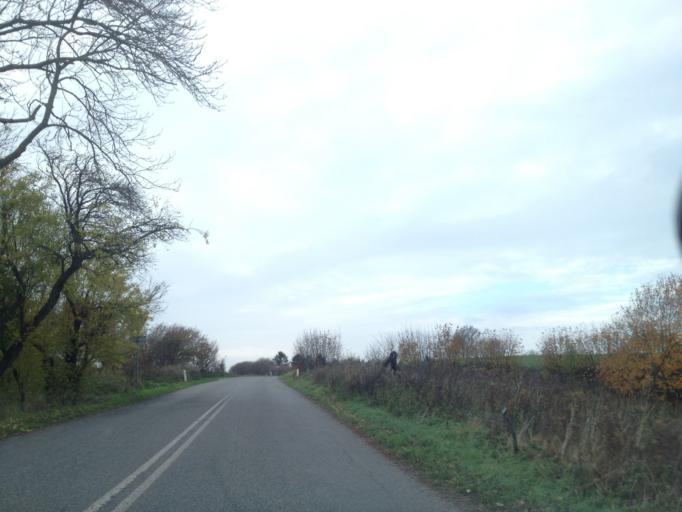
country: DK
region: South Denmark
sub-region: Assens Kommune
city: Vissenbjerg
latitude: 55.4039
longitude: 10.1587
